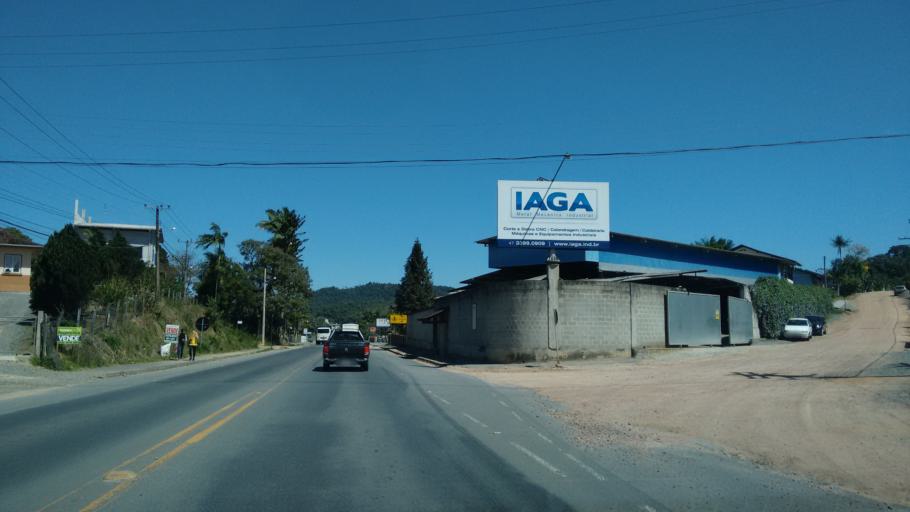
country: BR
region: Santa Catarina
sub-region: Pomerode
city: Pomerode
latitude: -26.8254
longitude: -49.1596
